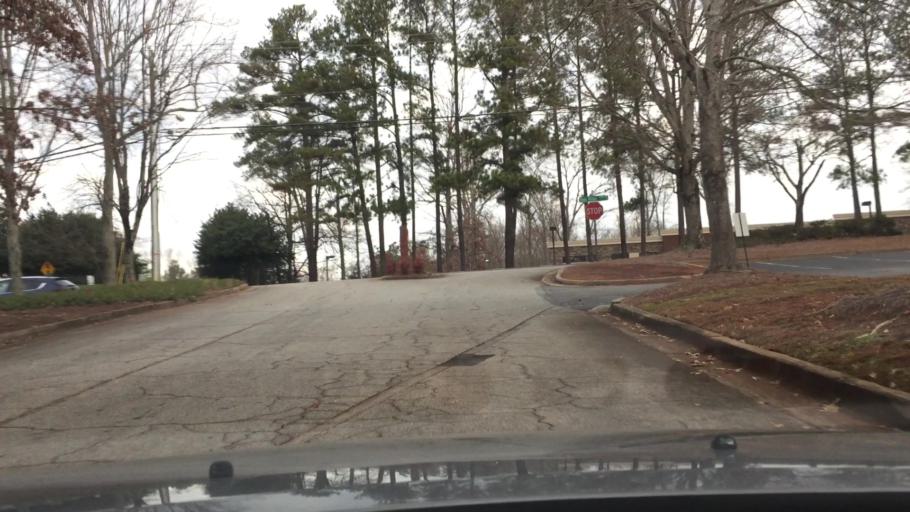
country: US
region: Georgia
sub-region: Gwinnett County
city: Norcross
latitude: 33.9542
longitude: -84.2175
